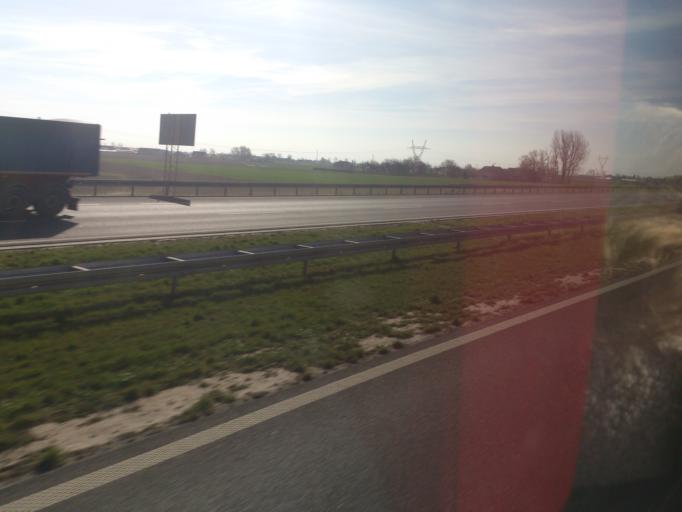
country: PL
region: Kujawsko-Pomorskie
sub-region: Powiat aleksandrowski
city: Waganiec
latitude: 52.7571
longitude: 18.8570
